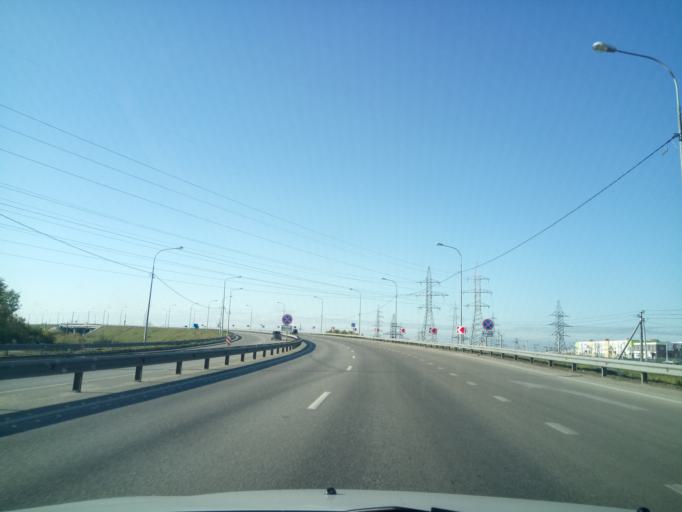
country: RU
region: Nizjnij Novgorod
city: Burevestnik
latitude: 56.1816
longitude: 43.9156
